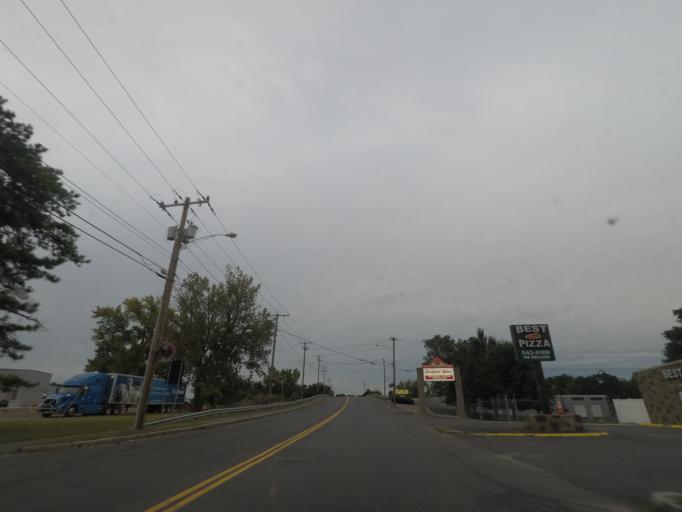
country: US
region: Massachusetts
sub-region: Hampden County
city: Ludlow
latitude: 42.1470
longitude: -72.5036
